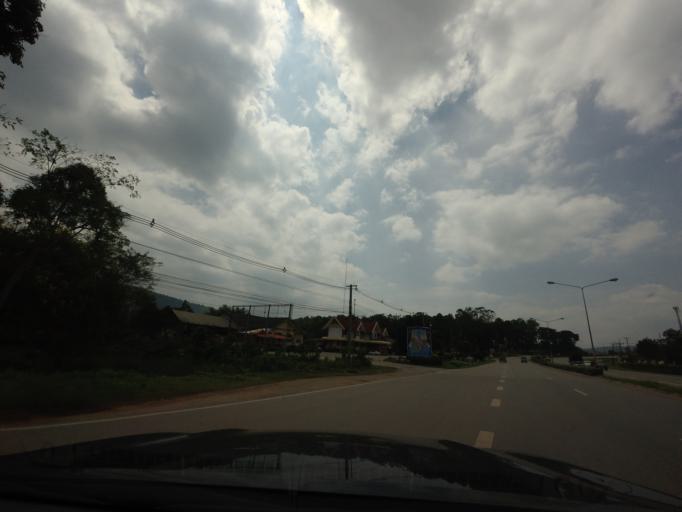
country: TH
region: Loei
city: Phu Ruea
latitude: 17.4493
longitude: 101.3563
